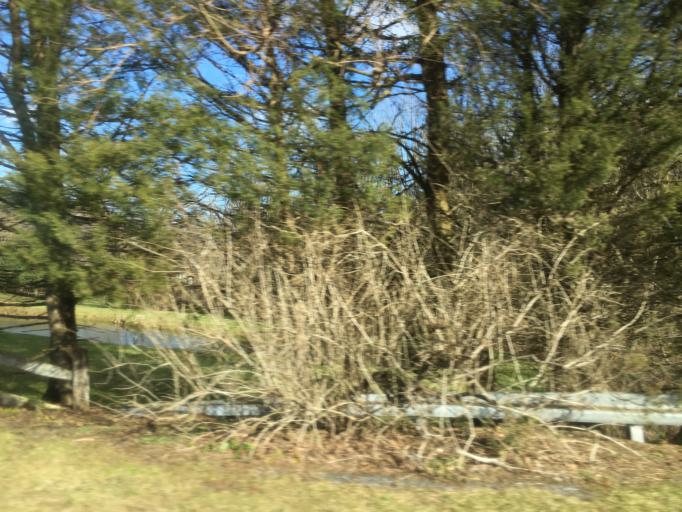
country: US
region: Pennsylvania
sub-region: Lehigh County
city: Egypt
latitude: 40.6880
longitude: -75.5507
